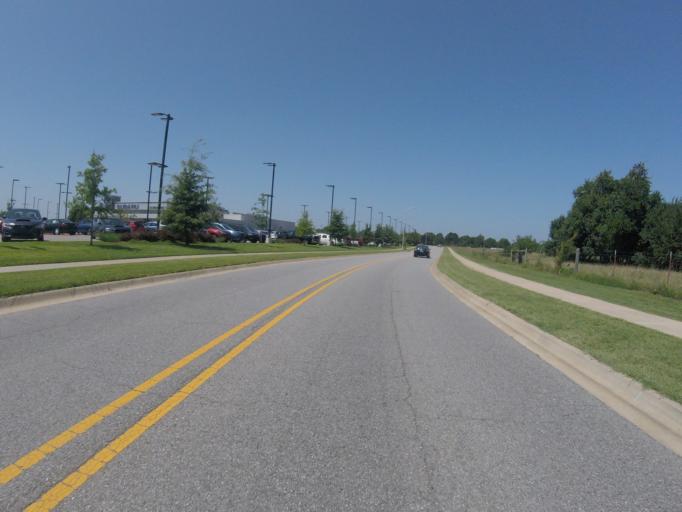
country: US
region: Arkansas
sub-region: Washington County
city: Fayetteville
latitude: 36.0941
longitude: -94.1906
